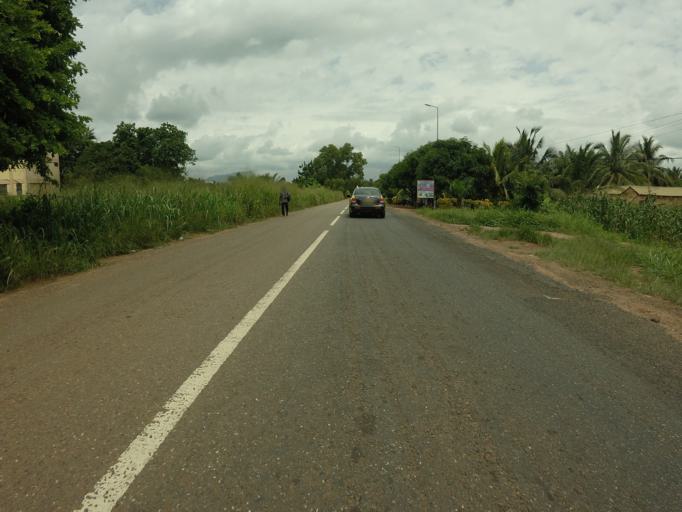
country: GH
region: Volta
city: Ho
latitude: 6.5862
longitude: 0.4630
